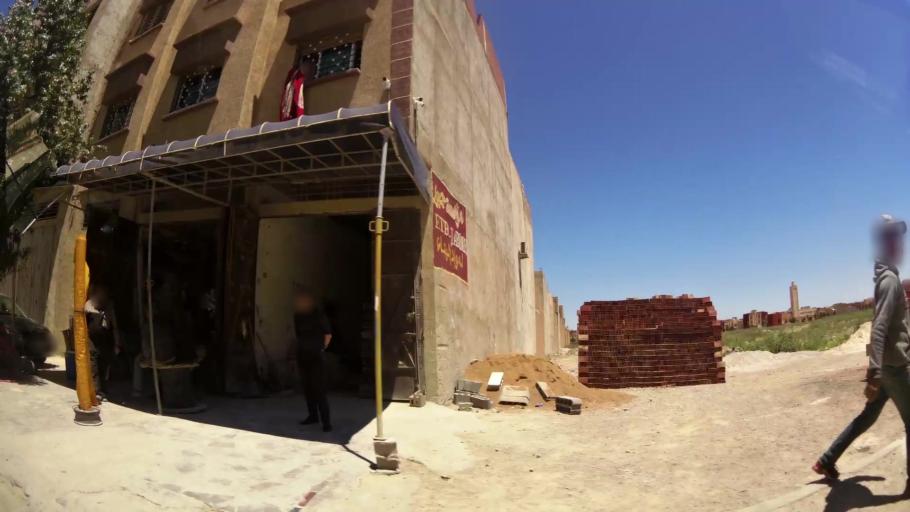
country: MA
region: Oriental
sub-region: Oujda-Angad
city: Oujda
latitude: 34.6779
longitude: -1.8721
